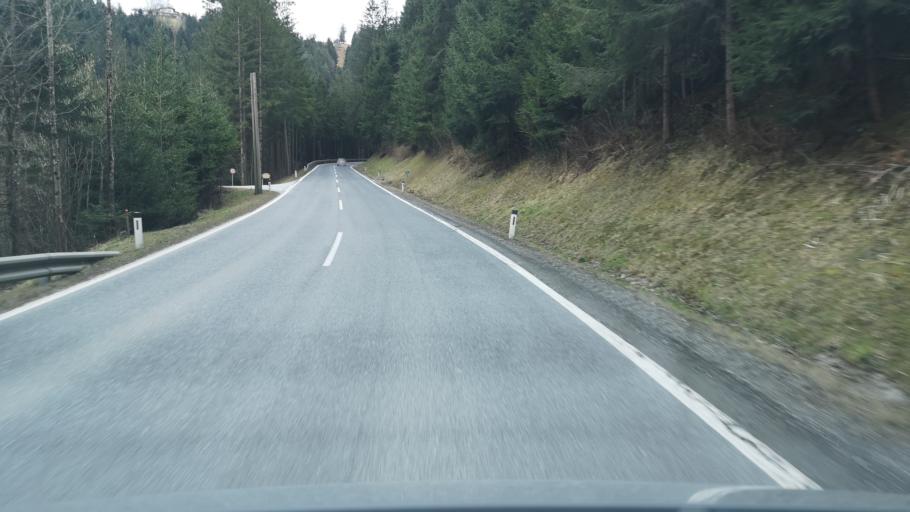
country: AT
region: Styria
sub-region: Politischer Bezirk Weiz
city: Birkfeld
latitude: 47.3426
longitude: 15.6979
